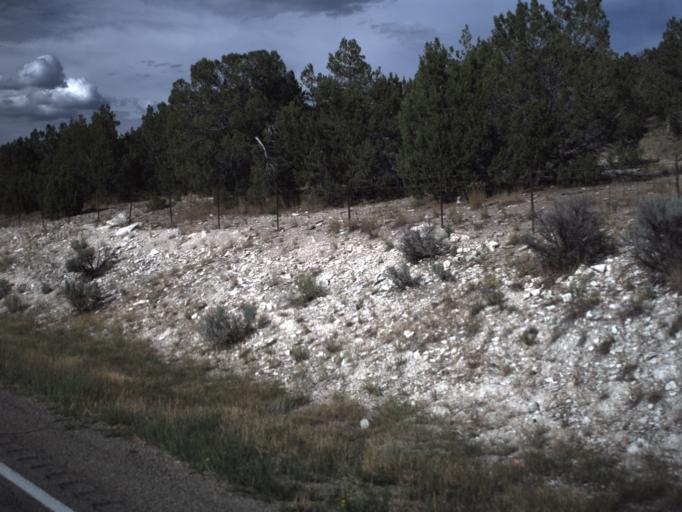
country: US
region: Utah
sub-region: Sanpete County
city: Fairview
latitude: 39.6514
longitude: -111.4509
